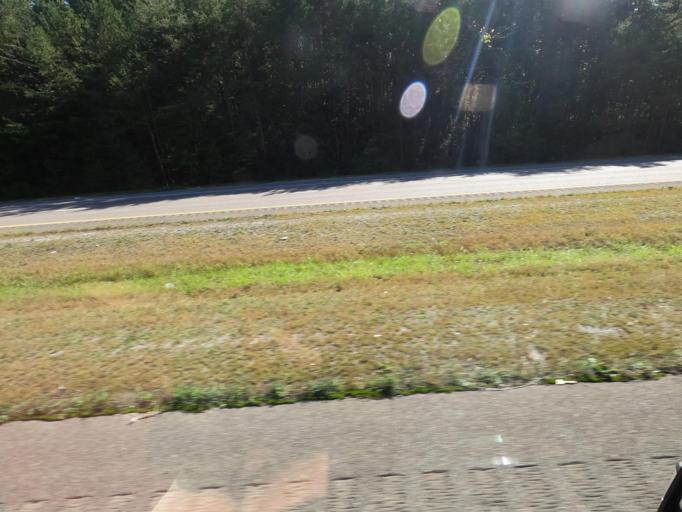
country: US
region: Tennessee
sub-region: Hamilton County
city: Sale Creek
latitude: 35.3141
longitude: -85.1399
